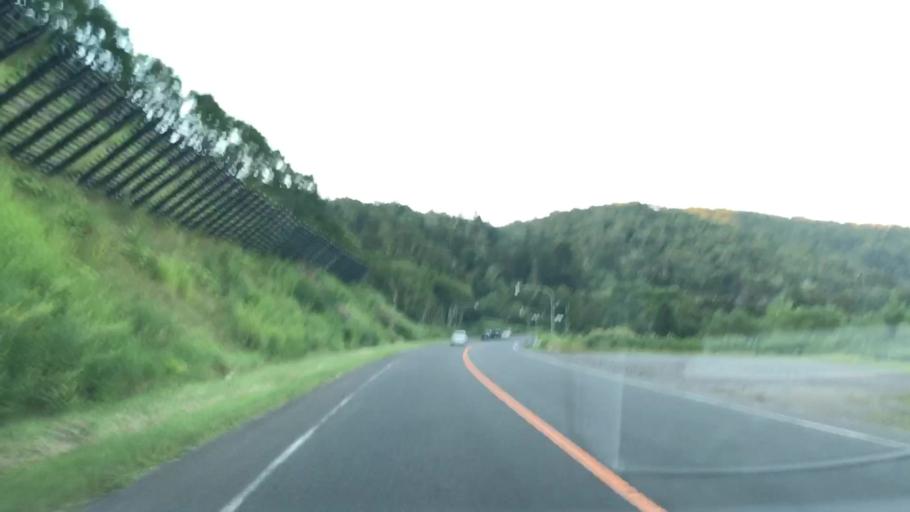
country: JP
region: Hokkaido
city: Sapporo
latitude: 42.8692
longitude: 141.1120
